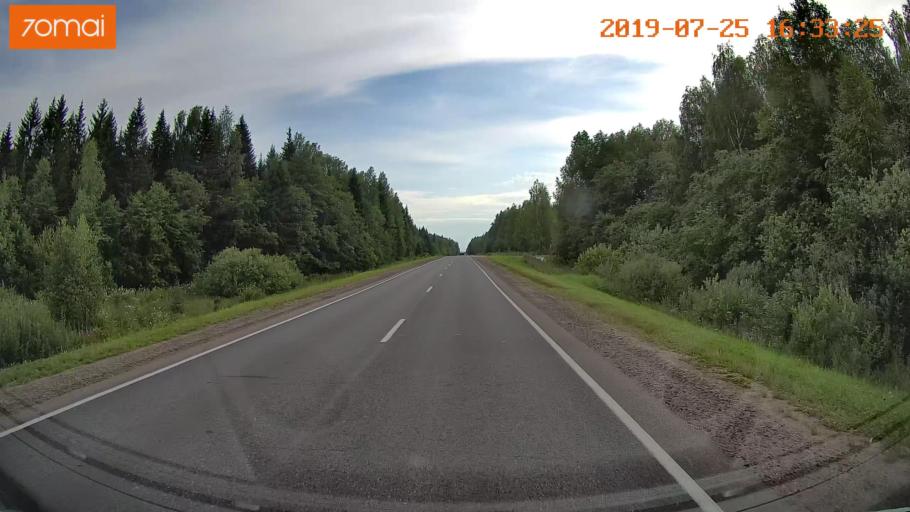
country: RU
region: Ivanovo
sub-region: Privolzhskiy Rayon
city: Ples
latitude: 57.4274
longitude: 41.4570
